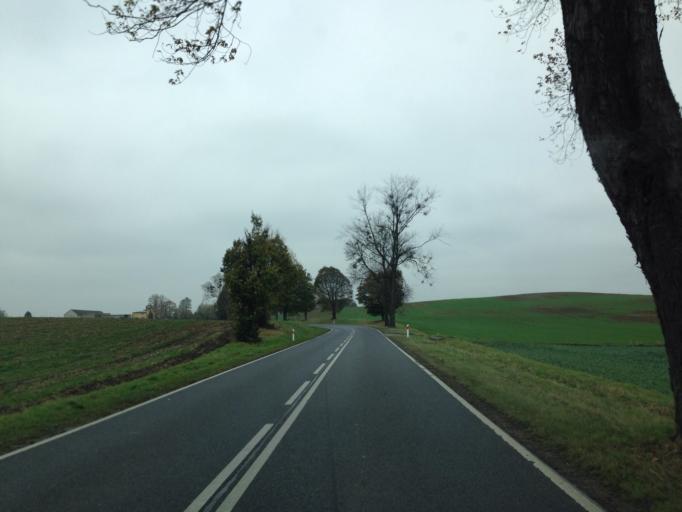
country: PL
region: Kujawsko-Pomorskie
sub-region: Powiat wabrzeski
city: Ksiazki
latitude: 53.3780
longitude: 19.0497
